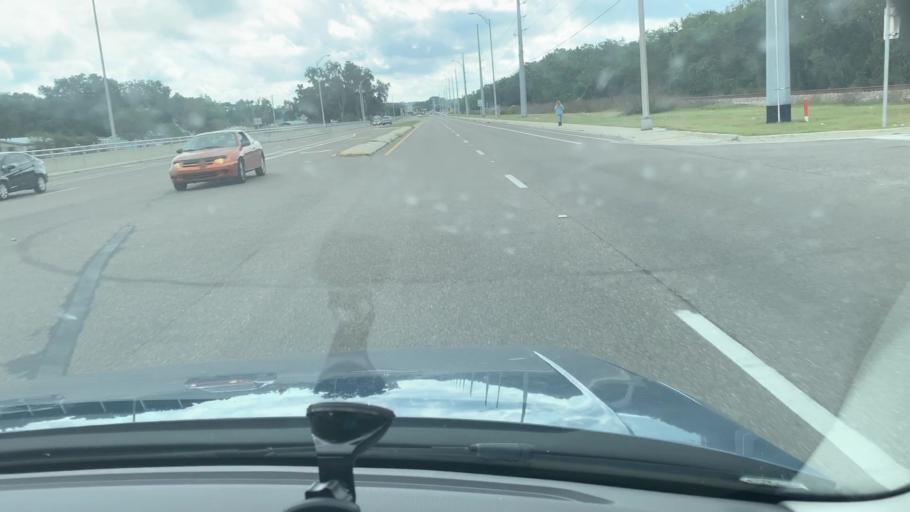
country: US
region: Florida
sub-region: Polk County
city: Kathleen
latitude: 28.1052
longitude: -82.0133
